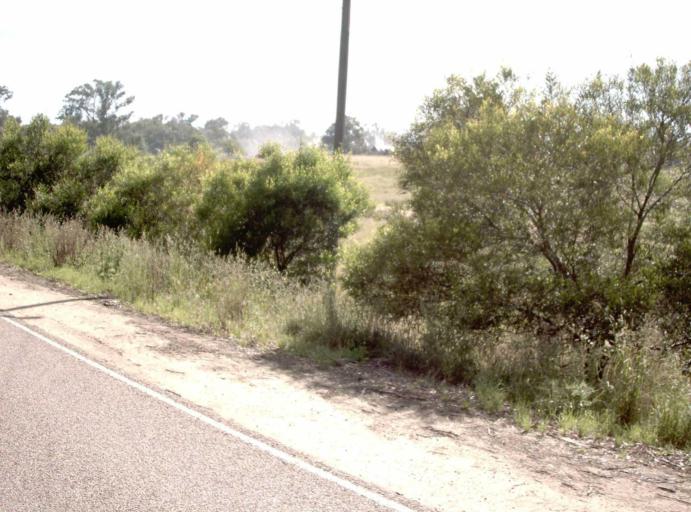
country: AU
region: Victoria
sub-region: East Gippsland
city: Lakes Entrance
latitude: -37.5310
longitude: 148.1535
